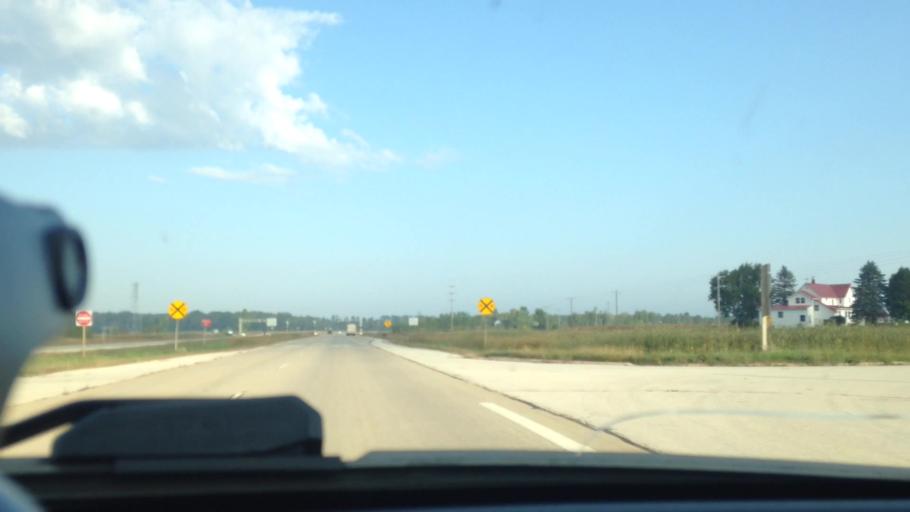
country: US
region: Wisconsin
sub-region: Oconto County
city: Oconto Falls
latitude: 44.9797
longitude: -88.0439
